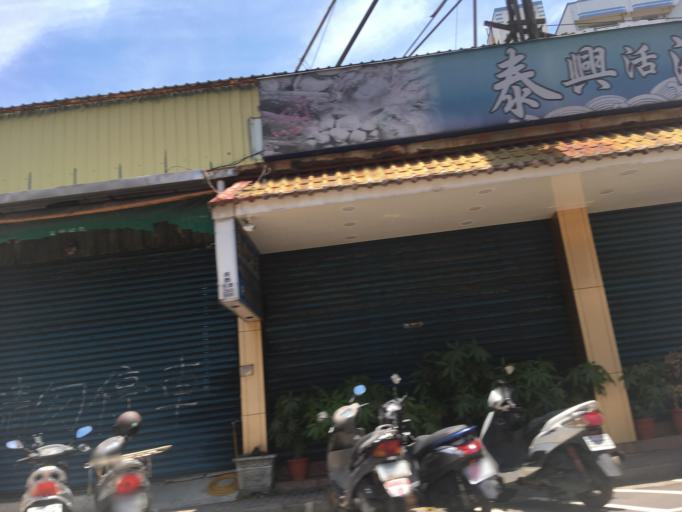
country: TW
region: Taipei
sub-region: Taipei
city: Banqiao
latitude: 25.0545
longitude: 121.4306
